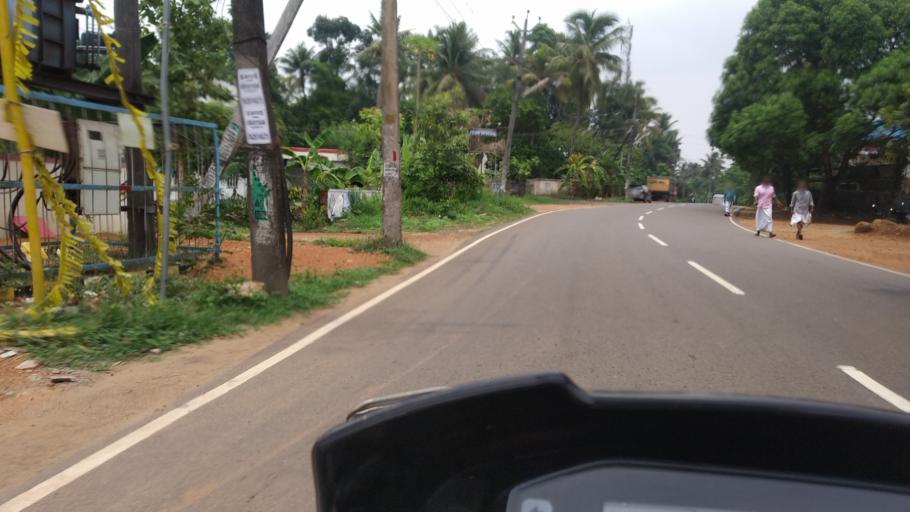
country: IN
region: Kerala
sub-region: Ernakulam
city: Aluva
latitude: 10.1558
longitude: 76.3316
